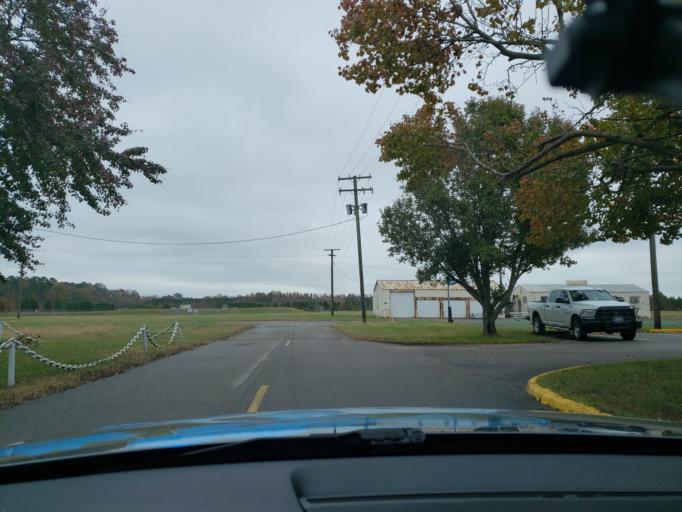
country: US
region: Virginia
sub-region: City of Chesapeake
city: Chesapeake
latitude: 36.7059
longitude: -76.1280
